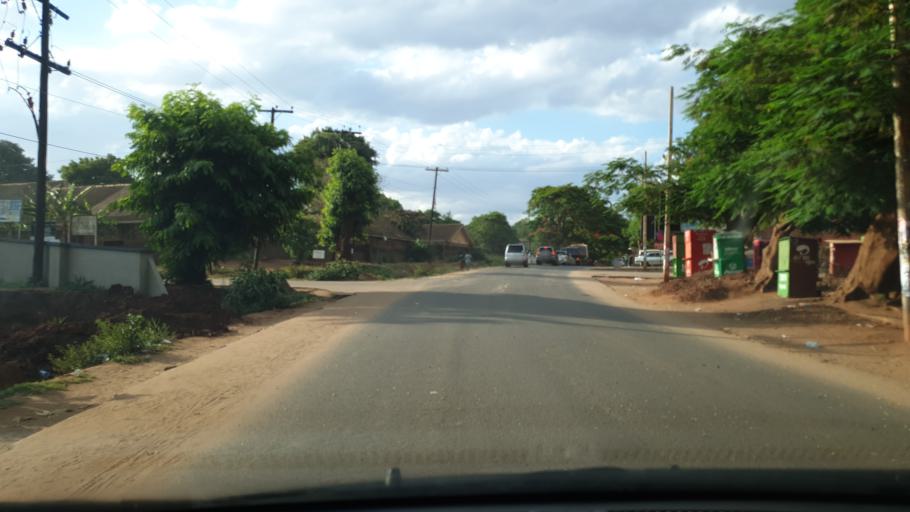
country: MW
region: Central Region
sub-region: Lilongwe District
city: Lilongwe
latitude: -13.9892
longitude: 33.7662
